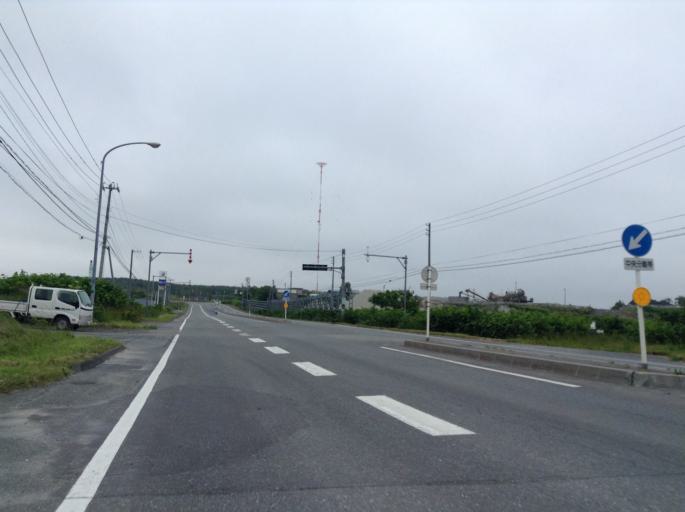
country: JP
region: Hokkaido
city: Wakkanai
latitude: 45.3791
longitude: 141.7105
